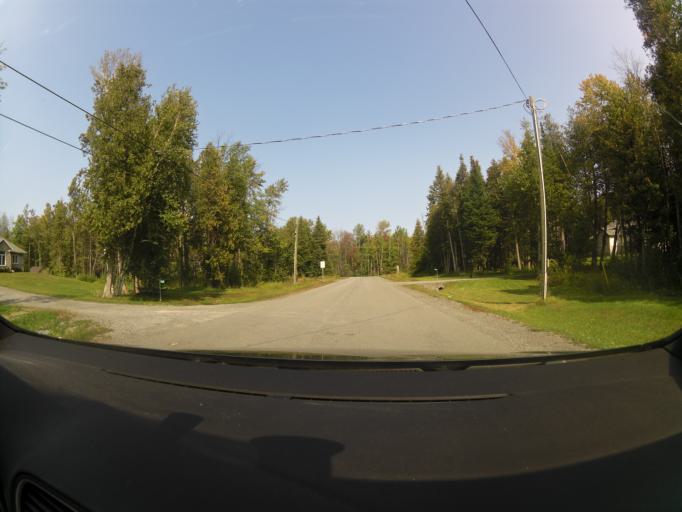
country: CA
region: Ontario
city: Carleton Place
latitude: 45.3274
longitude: -76.1553
